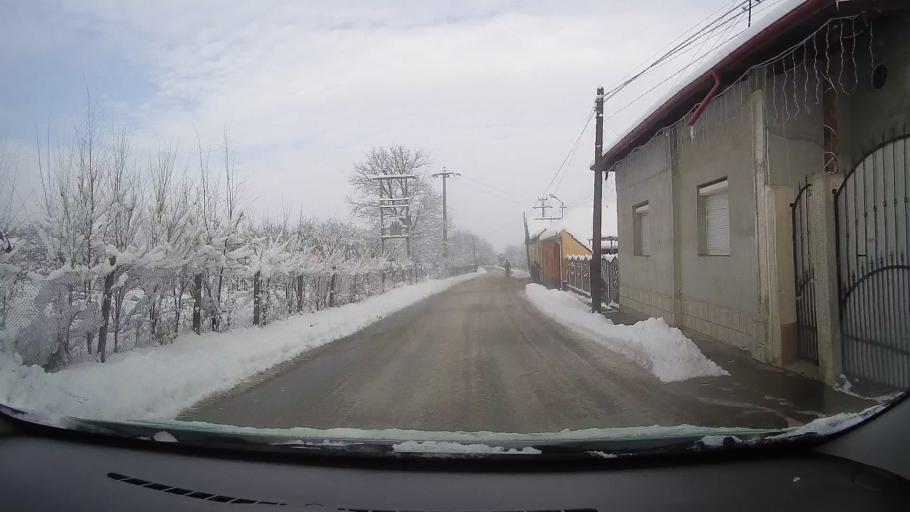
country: RO
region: Alba
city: Pianu de Sus
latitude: 45.9036
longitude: 23.4803
